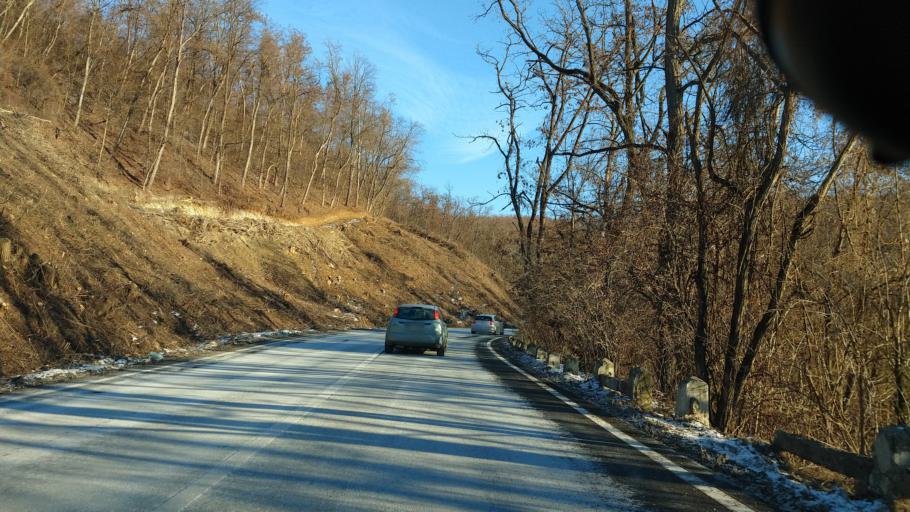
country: RO
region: Bacau
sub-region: Comuna Luizi-Calugara
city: Luizi-Calugara
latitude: 46.5433
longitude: 26.8184
